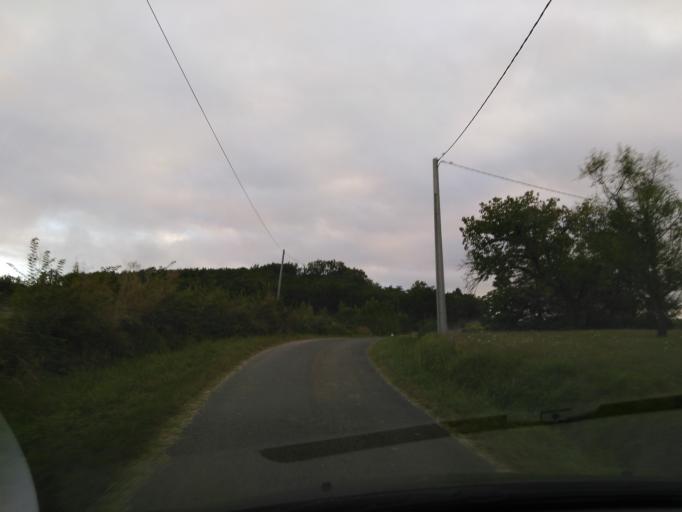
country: FR
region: Aquitaine
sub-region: Departement du Lot-et-Garonne
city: Saint-Hilaire
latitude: 44.5074
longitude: 0.6820
